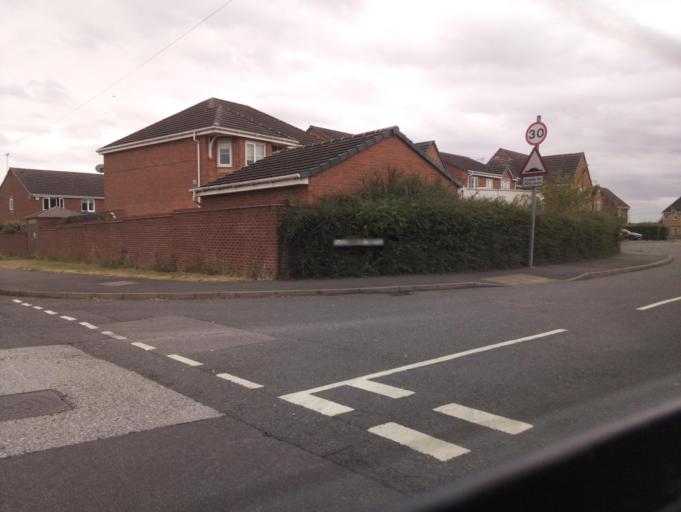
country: GB
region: England
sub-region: Derbyshire
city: Borrowash
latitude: 52.9100
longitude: -1.3937
